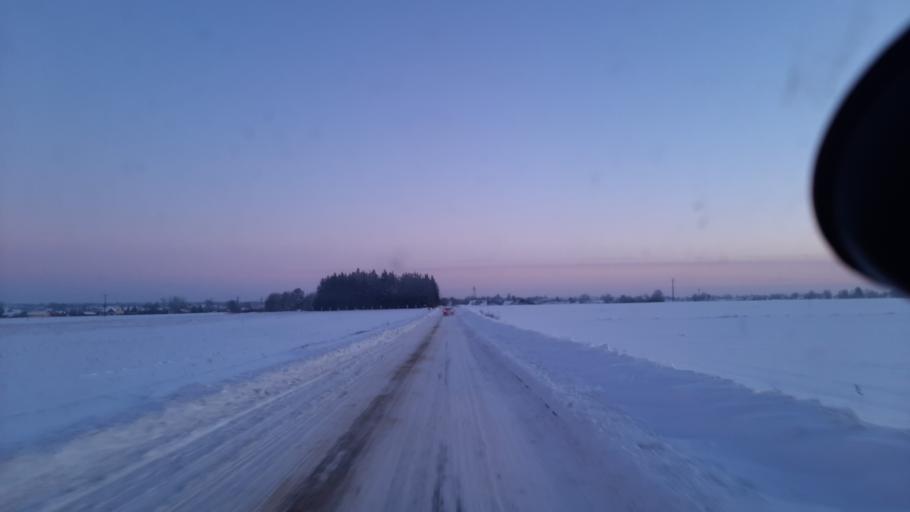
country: PL
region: Lublin Voivodeship
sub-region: Powiat lubelski
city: Jastkow
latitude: 51.3686
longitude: 22.5245
